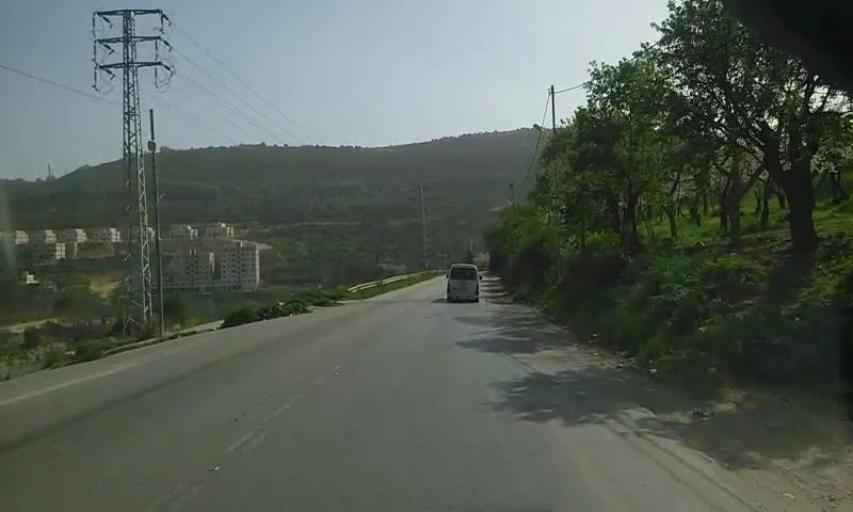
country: PS
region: West Bank
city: Dura al Qar`
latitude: 31.9713
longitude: 35.2297
